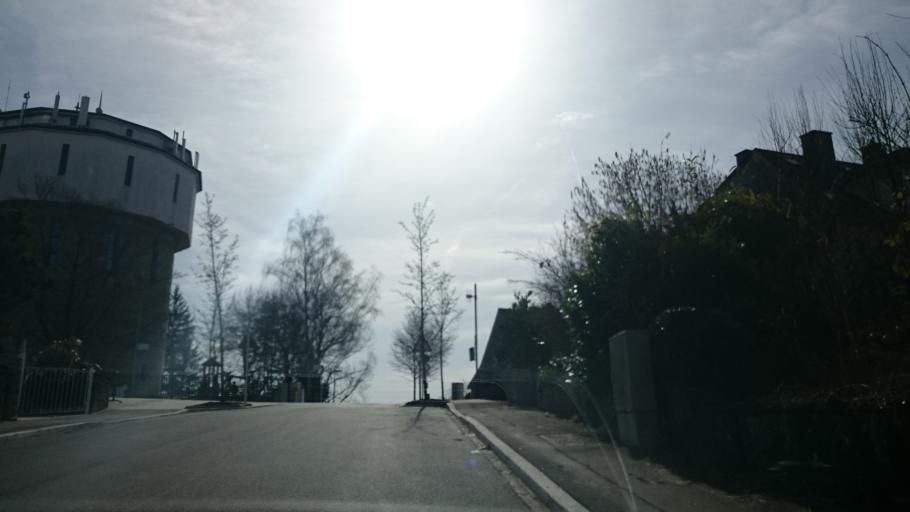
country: LU
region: Luxembourg
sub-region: Canton de Luxembourg
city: Luxembourg
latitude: 49.5870
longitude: 6.1084
